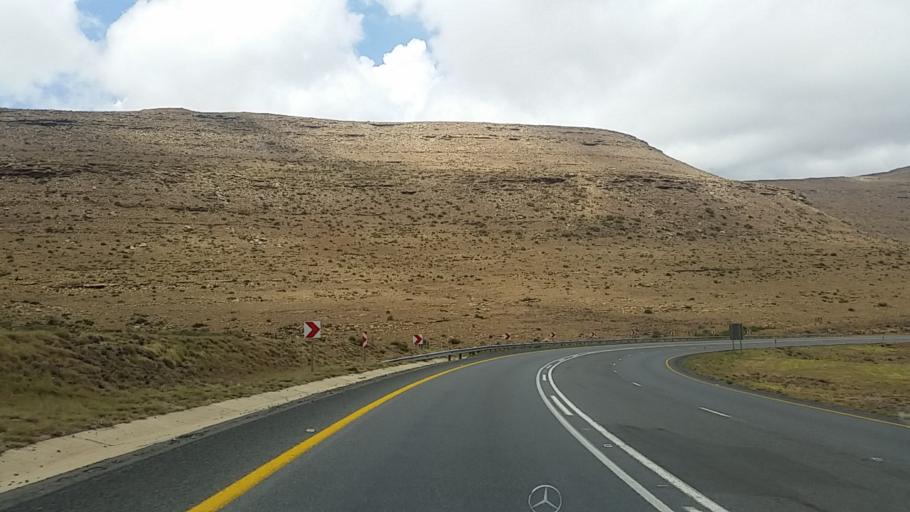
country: ZA
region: Eastern Cape
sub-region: Chris Hani District Municipality
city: Middelburg
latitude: -31.8454
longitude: 24.8801
